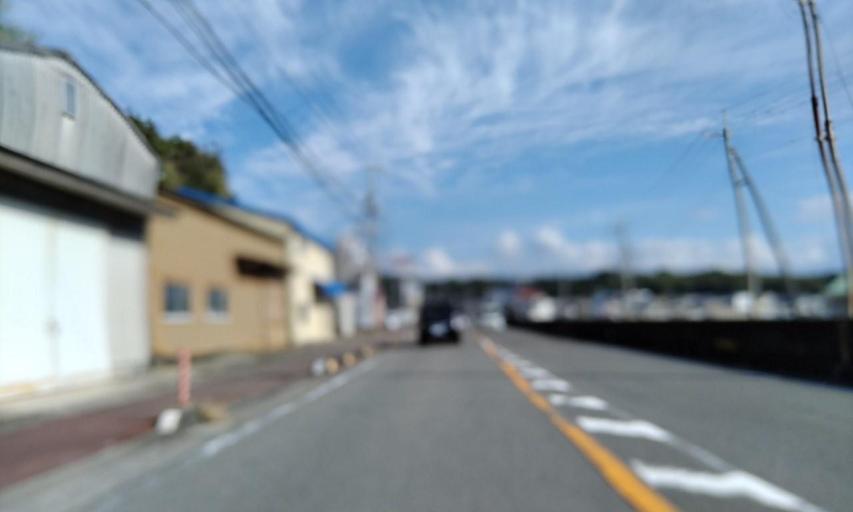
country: JP
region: Wakayama
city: Gobo
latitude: 33.8144
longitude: 135.2151
